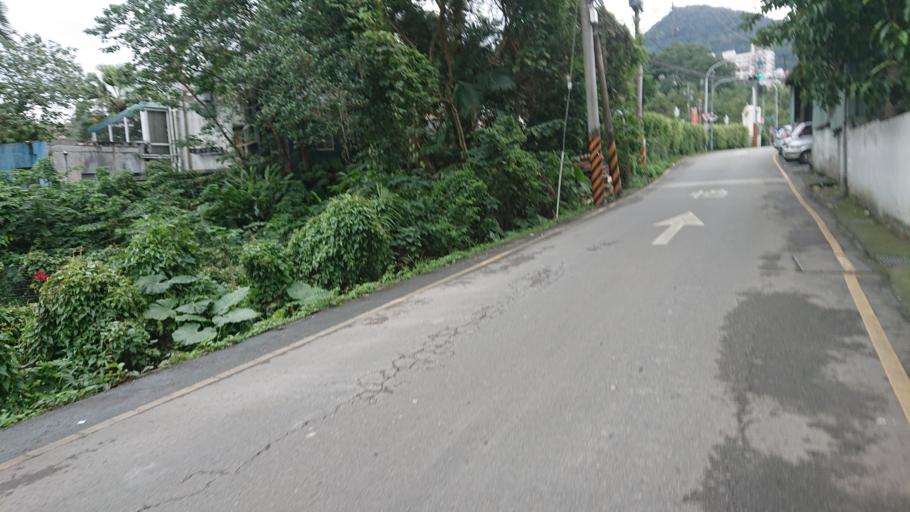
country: TW
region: Taipei
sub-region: Taipei
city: Banqiao
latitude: 24.9607
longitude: 121.4429
